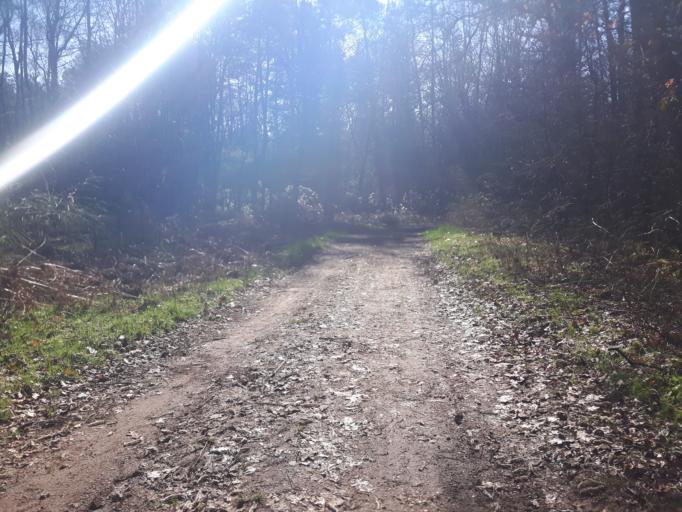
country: NL
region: Overijssel
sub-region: Gemeente Haaksbergen
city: Haaksbergen
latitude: 52.1682
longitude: 6.8168
